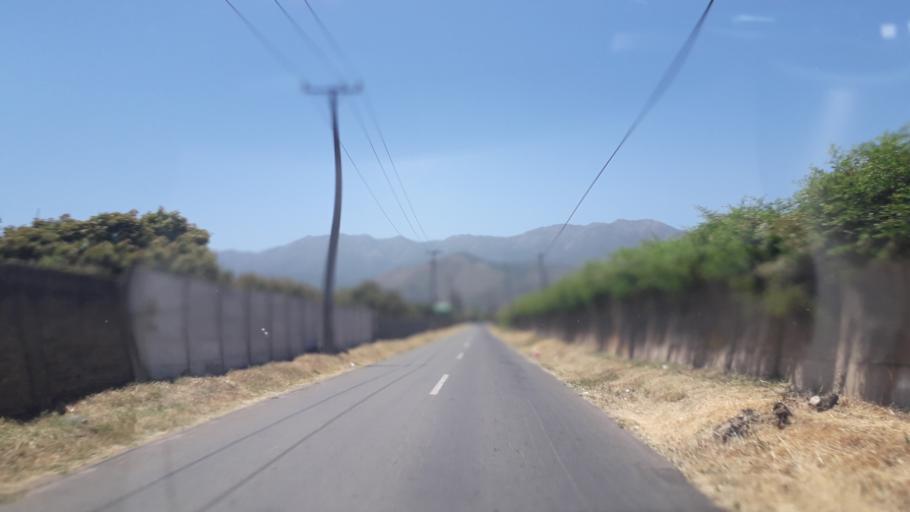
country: CL
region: Valparaiso
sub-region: Provincia de Quillota
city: Quillota
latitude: -32.9086
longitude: -71.2215
